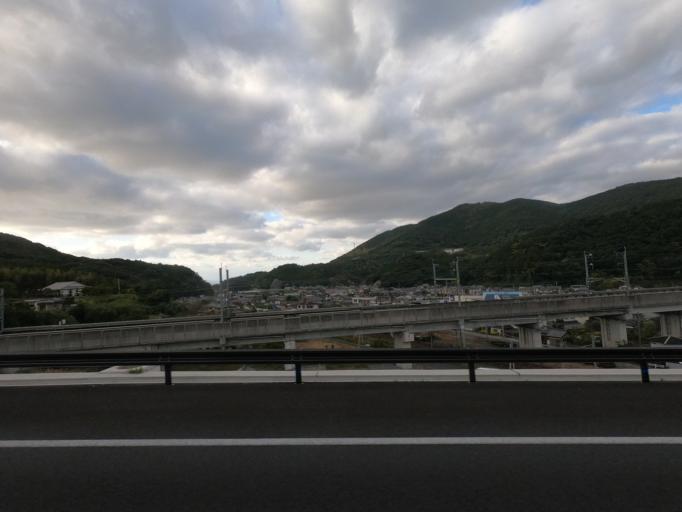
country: JP
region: Kumamoto
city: Minamata
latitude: 32.2315
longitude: 130.4515
